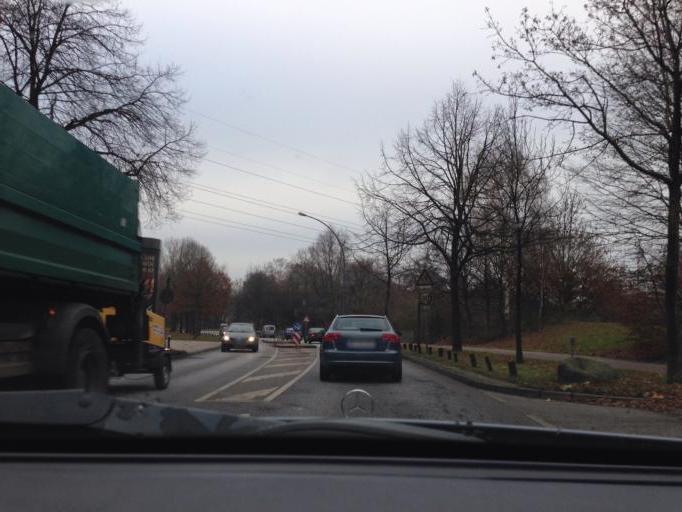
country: DE
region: Hamburg
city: Farmsen-Berne
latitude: 53.6045
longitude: 10.1238
